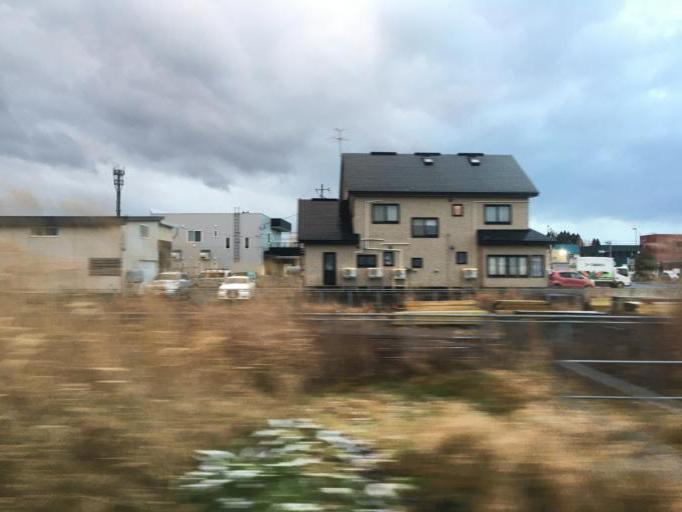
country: JP
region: Aomori
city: Aomori Shi
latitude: 40.8273
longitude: 140.6970
